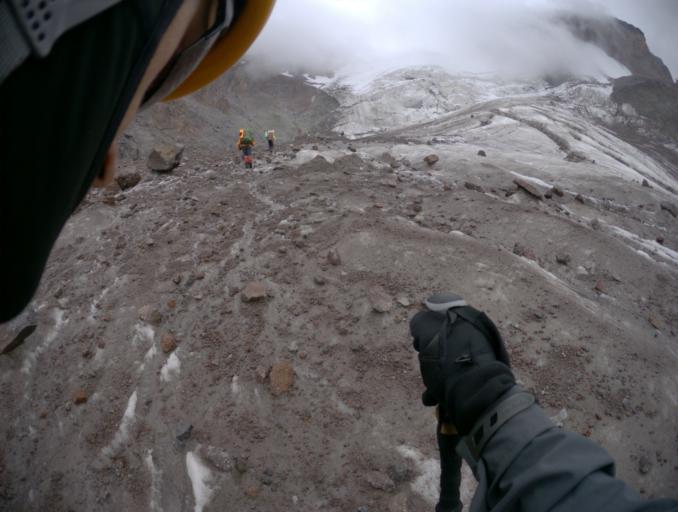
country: RU
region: Kabardino-Balkariya
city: Terskol
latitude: 43.3786
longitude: 42.4008
